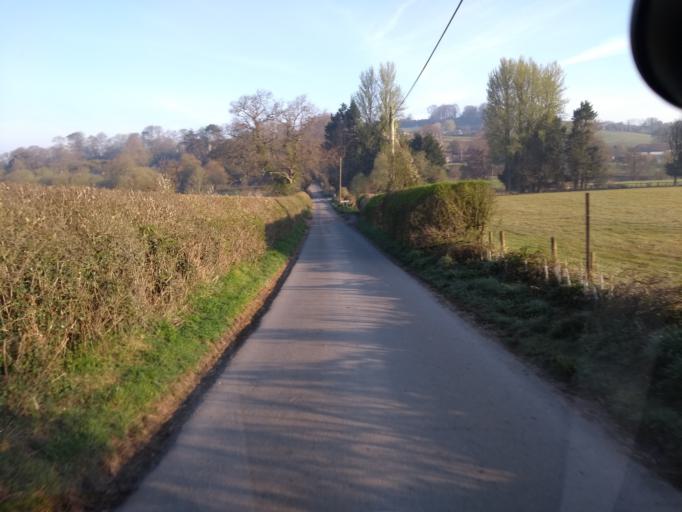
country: GB
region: England
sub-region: Somerset
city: Crewkerne
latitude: 50.8475
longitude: -2.8111
